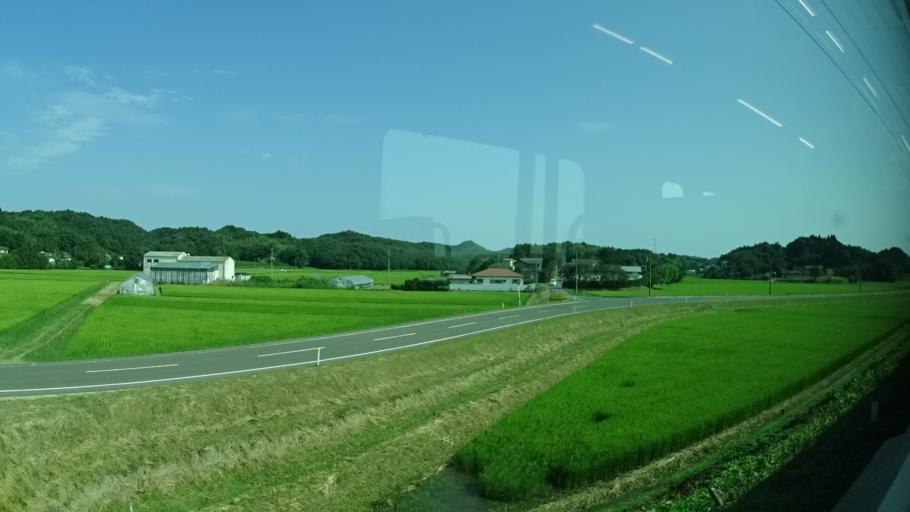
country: JP
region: Miyagi
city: Matsushima
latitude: 38.4416
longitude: 141.0890
